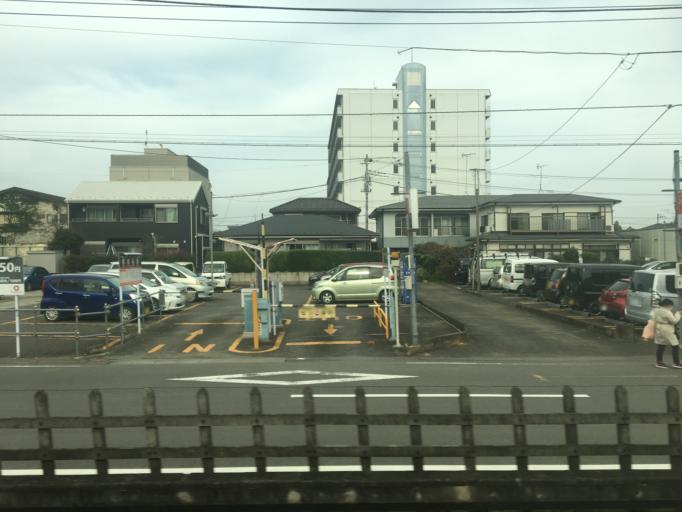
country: JP
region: Saitama
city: Sayama
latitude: 35.8724
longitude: 139.4314
